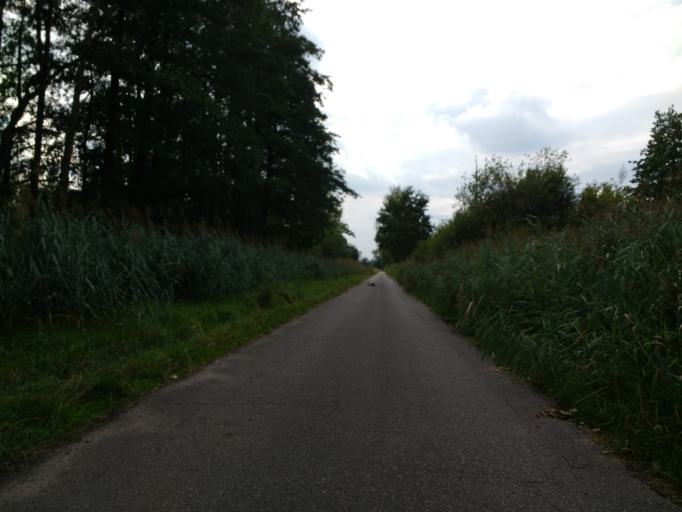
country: DE
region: Lower Saxony
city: Calberlah
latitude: 52.4259
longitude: 10.6615
